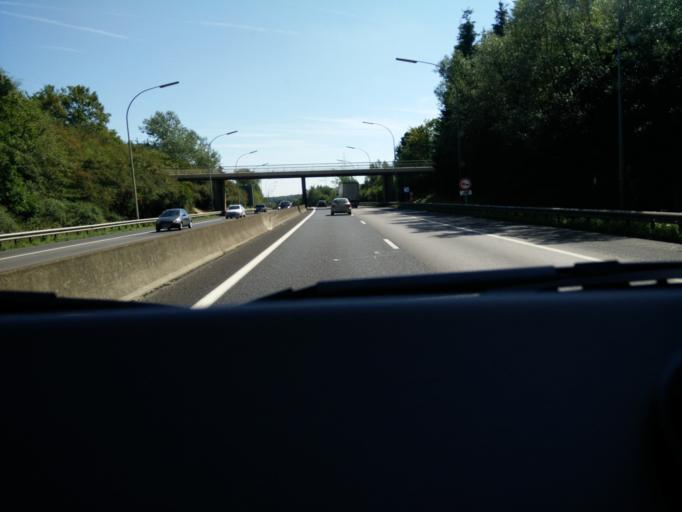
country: LU
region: Luxembourg
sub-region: Canton d'Esch-sur-Alzette
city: Leudelange
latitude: 49.5812
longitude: 6.0957
